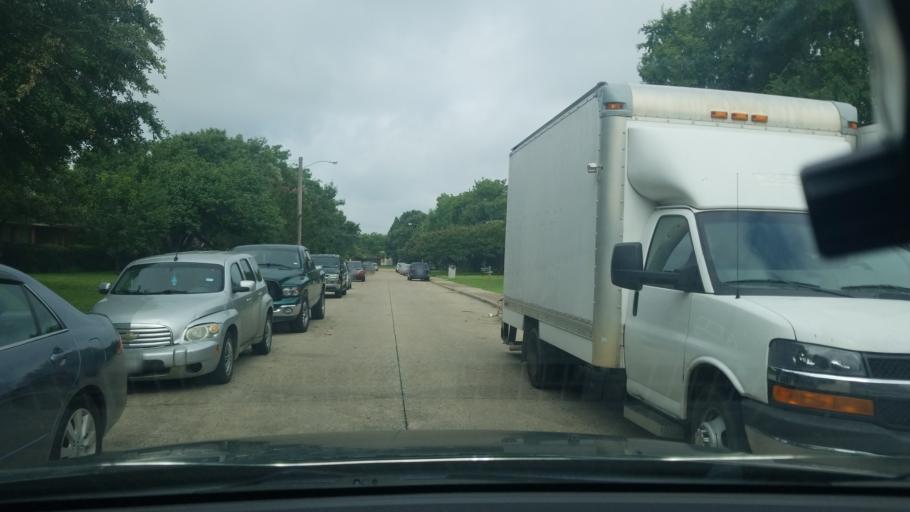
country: US
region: Texas
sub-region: Dallas County
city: Balch Springs
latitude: 32.7885
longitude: -96.6880
